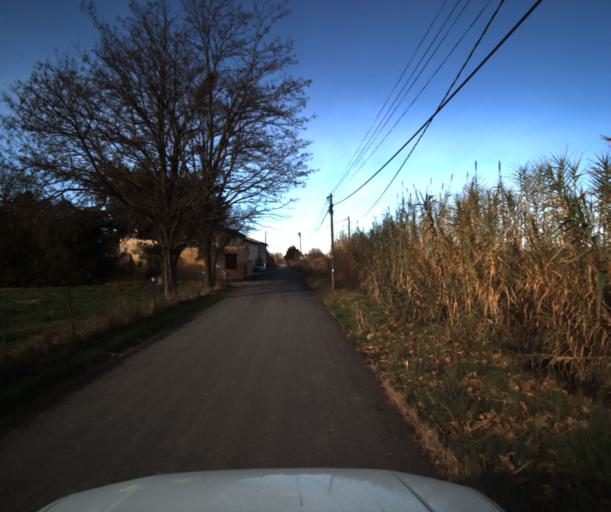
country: FR
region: Provence-Alpes-Cote d'Azur
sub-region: Departement des Bouches-du-Rhone
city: Le Puy-Sainte-Reparade
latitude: 43.6878
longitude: 5.4511
